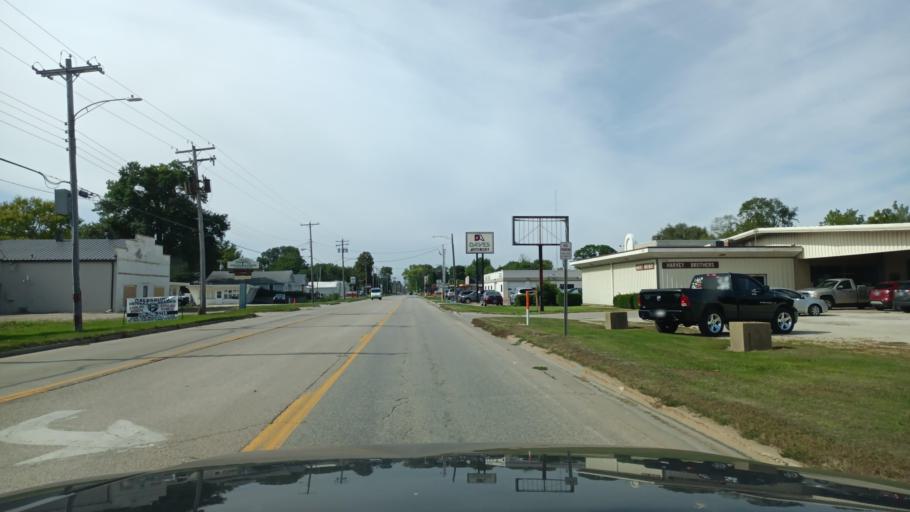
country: US
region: Illinois
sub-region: Knox County
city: Galesburg
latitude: 40.9356
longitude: -90.3374
